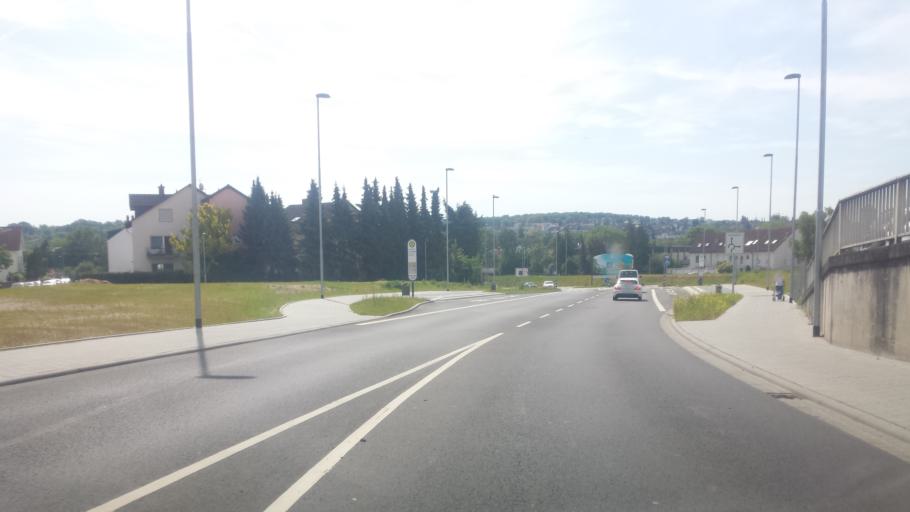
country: DE
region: Hesse
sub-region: Regierungsbezirk Darmstadt
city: Bad Vilbel
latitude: 50.1868
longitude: 8.7346
